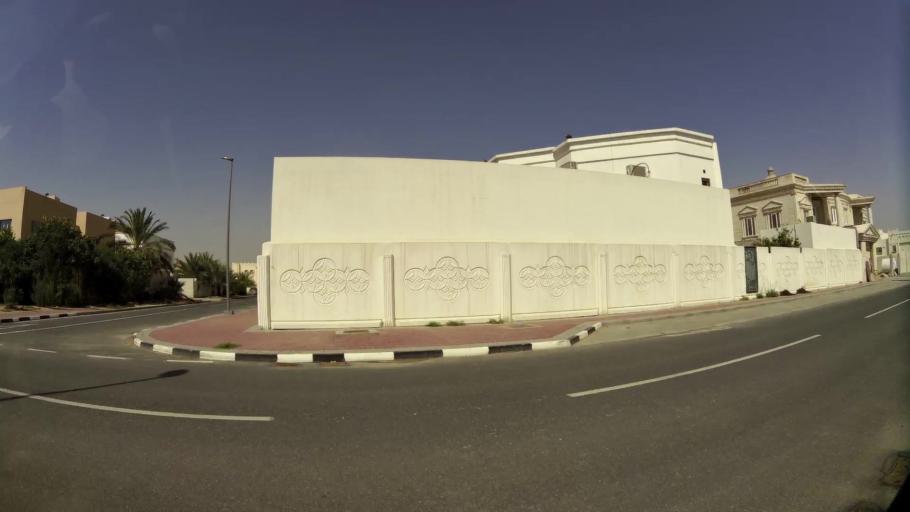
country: QA
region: Baladiyat ad Dawhah
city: Doha
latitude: 25.3547
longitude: 51.5152
